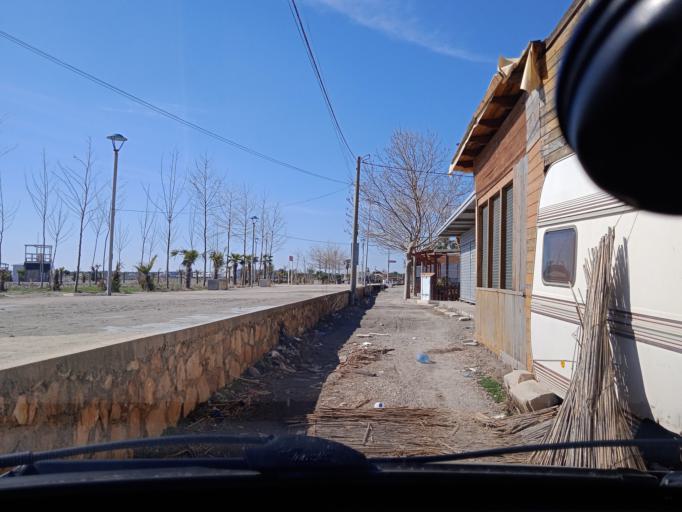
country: AL
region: Shkoder
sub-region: Rrethi i Shkodres
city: Velipoje
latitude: 41.8629
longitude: 19.4171
